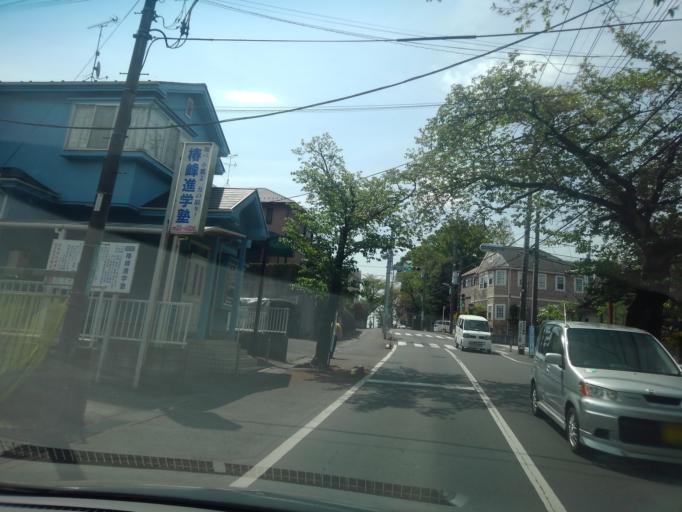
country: JP
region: Saitama
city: Tokorozawa
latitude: 35.7858
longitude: 139.4392
